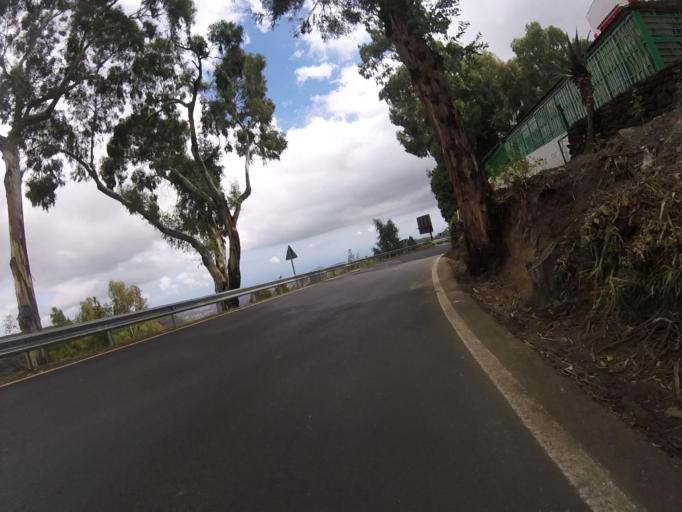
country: ES
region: Canary Islands
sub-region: Provincia de Las Palmas
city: Vega de San Mateo
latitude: 28.0014
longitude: -15.5698
